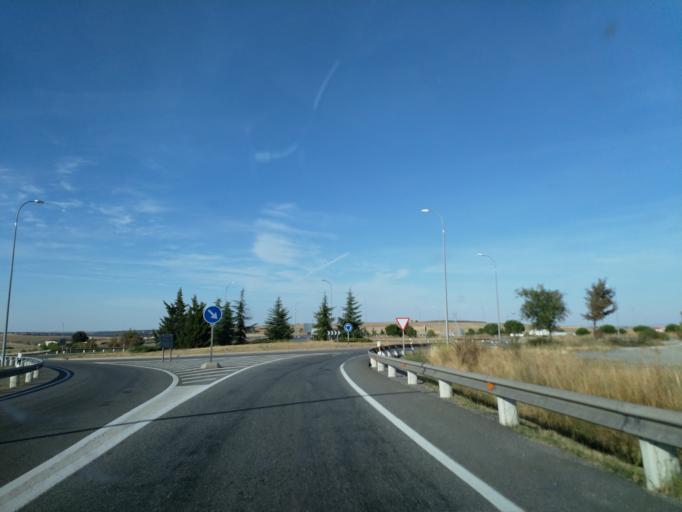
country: ES
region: Castille and Leon
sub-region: Provincia de Segovia
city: Villacastin
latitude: 40.7820
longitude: -4.4214
